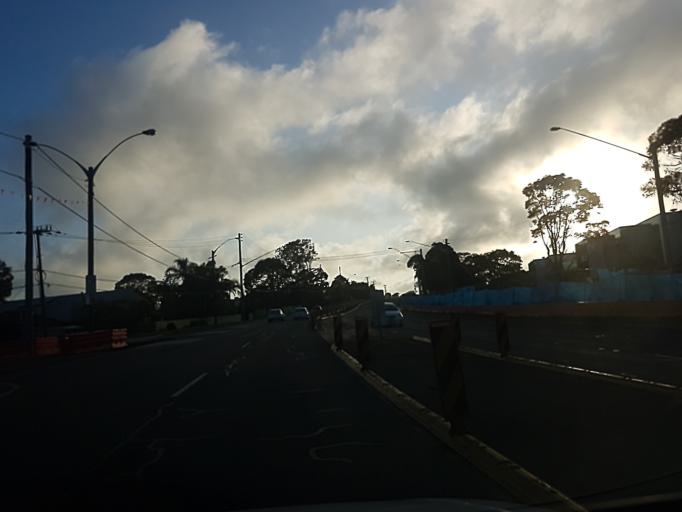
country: AU
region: New South Wales
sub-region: Warringah
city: Allambie Heights
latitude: -33.7517
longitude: 151.2456
